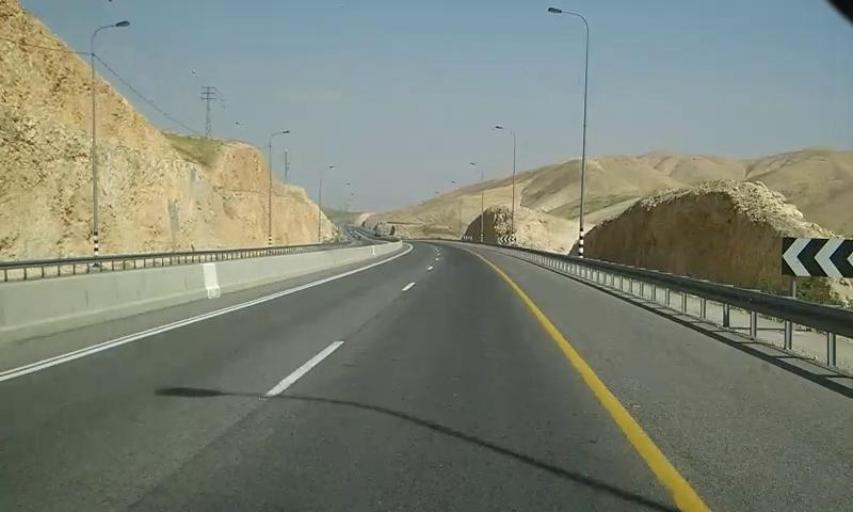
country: PS
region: West Bank
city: Jericho
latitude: 31.8160
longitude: 35.3708
